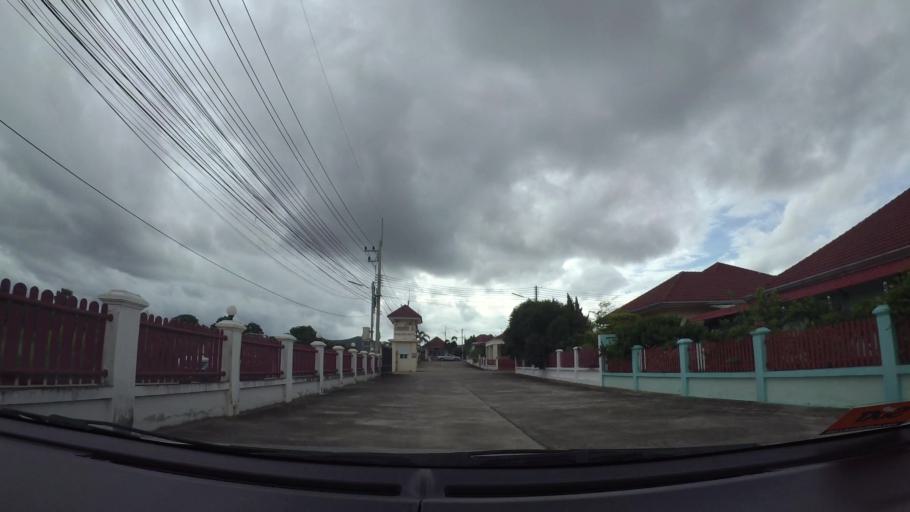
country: TH
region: Chon Buri
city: Sattahip
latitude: 12.7230
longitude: 100.9052
